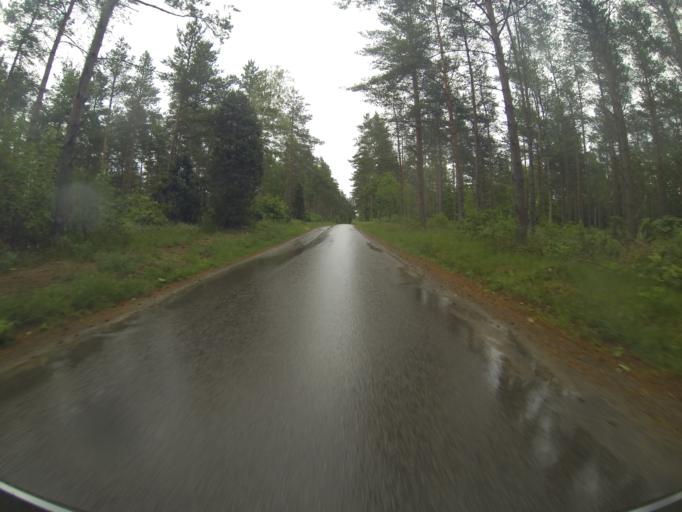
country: SE
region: Blekinge
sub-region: Ronneby Kommun
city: Ronneby
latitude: 56.1696
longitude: 15.3148
